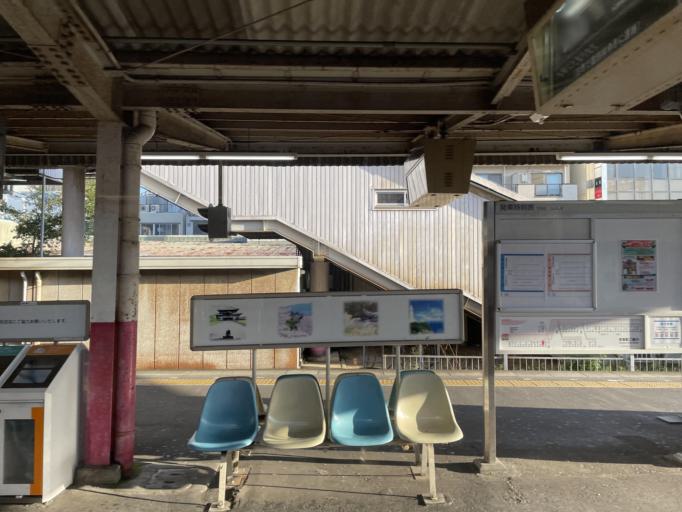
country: JP
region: Osaka
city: Kashihara
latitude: 34.5716
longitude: 135.5945
